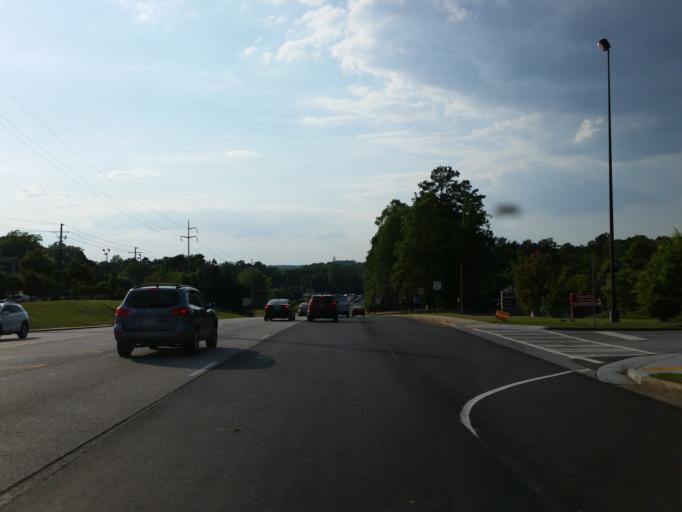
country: US
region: Georgia
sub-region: Cobb County
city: Smyrna
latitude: 33.8446
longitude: -84.5019
